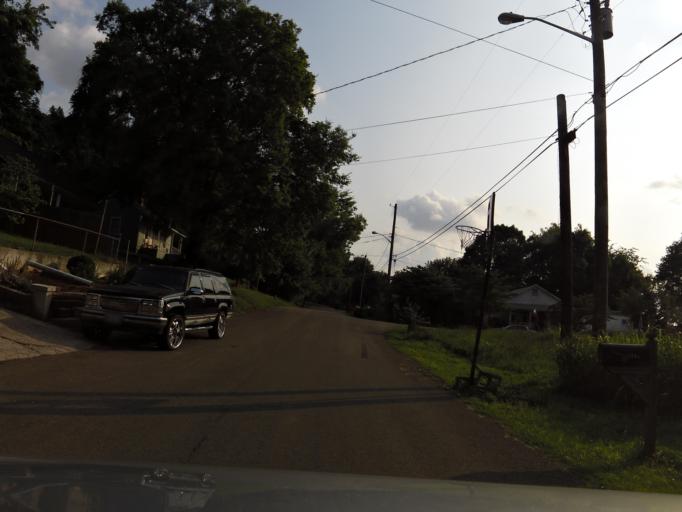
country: US
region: Tennessee
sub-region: Knox County
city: Knoxville
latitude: 35.9812
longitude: -83.9495
